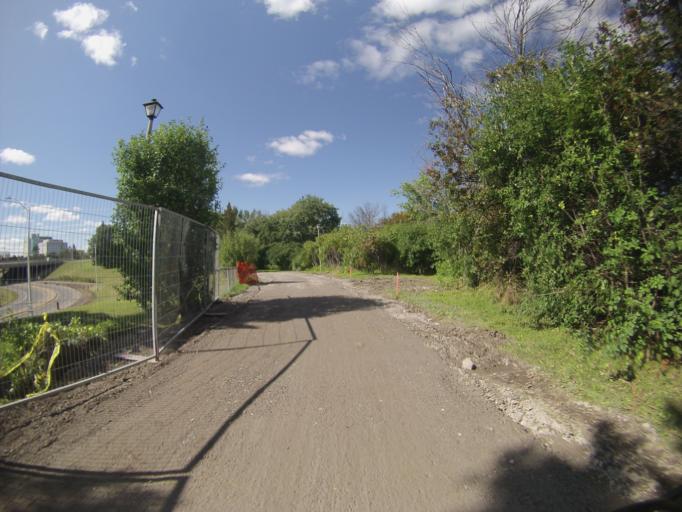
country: CA
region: Ontario
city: Ottawa
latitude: 45.3746
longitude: -75.6811
